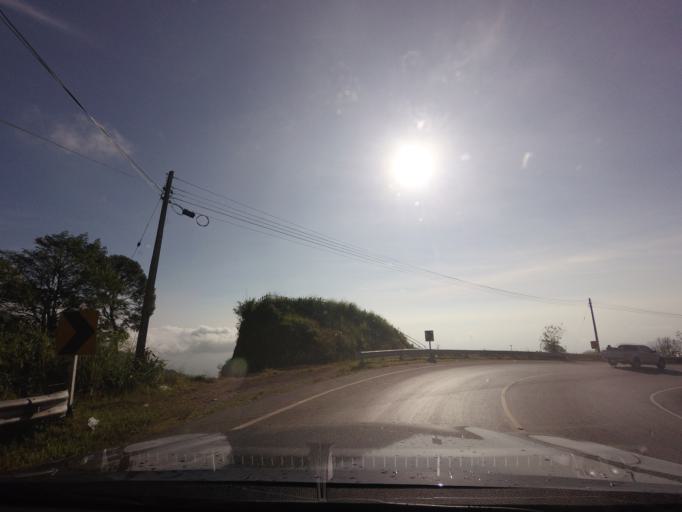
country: TH
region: Phetchabun
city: Lom Kao
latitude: 16.8859
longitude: 101.0985
